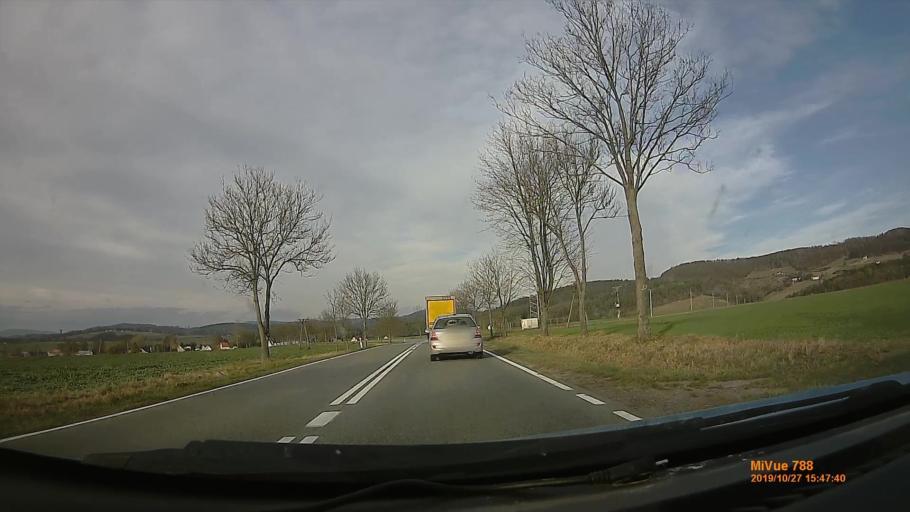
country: PL
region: Lower Silesian Voivodeship
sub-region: Powiat klodzki
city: Bozkow
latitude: 50.4911
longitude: 16.5865
